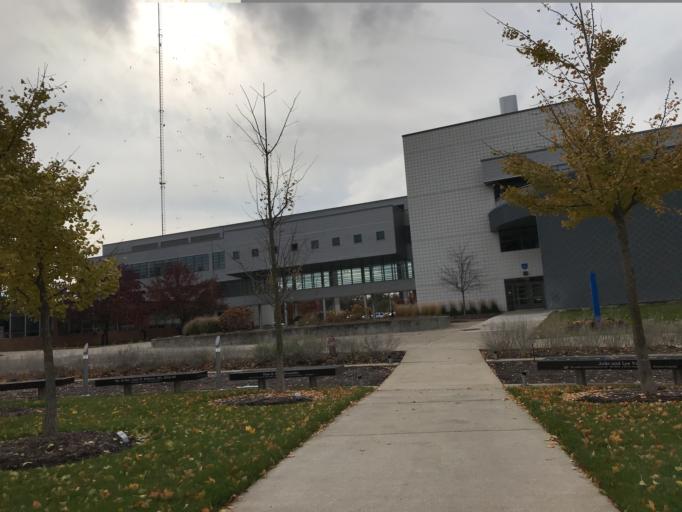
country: US
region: Michigan
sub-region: Oakland County
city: Southfield
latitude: 42.4746
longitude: -83.2495
